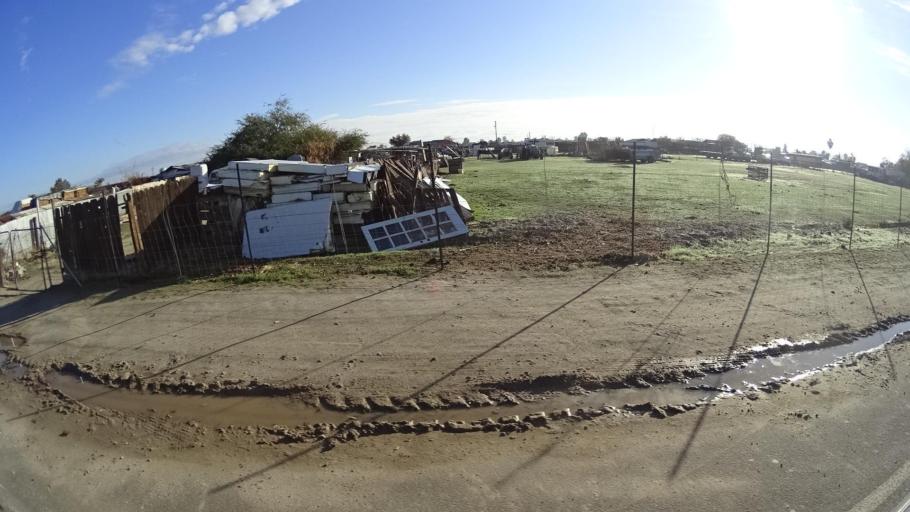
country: US
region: California
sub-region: Kern County
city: Delano
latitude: 35.7711
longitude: -119.2830
